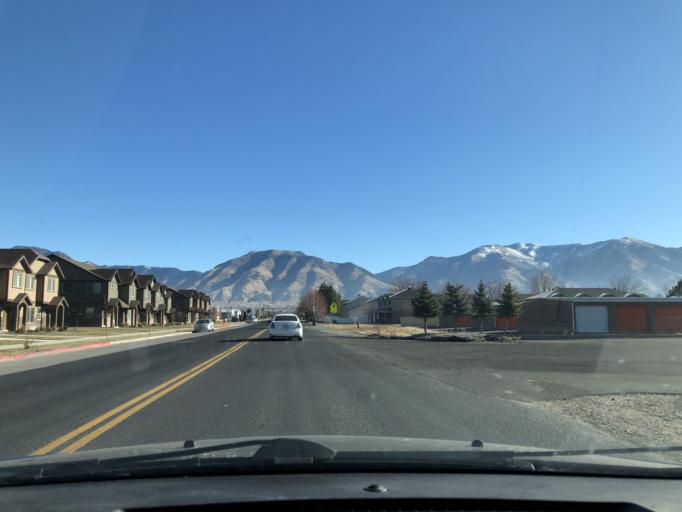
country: US
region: Utah
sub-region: Cache County
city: Logan
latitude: 41.7578
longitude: -111.8465
